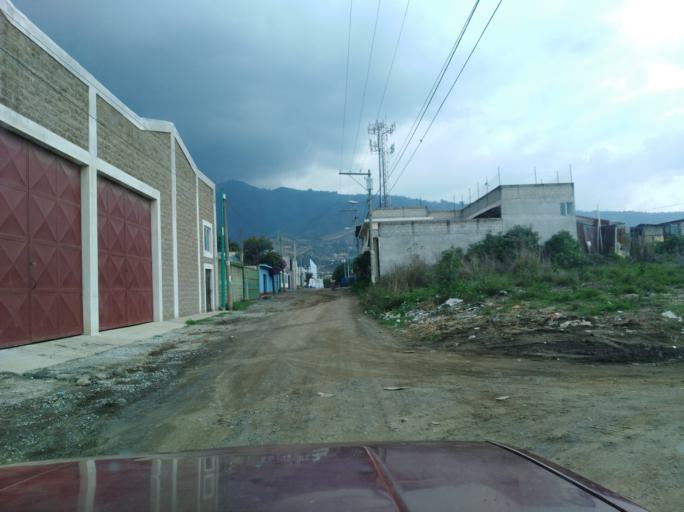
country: GT
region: Guatemala
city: Villa Nueva
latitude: 14.5240
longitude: -90.6227
